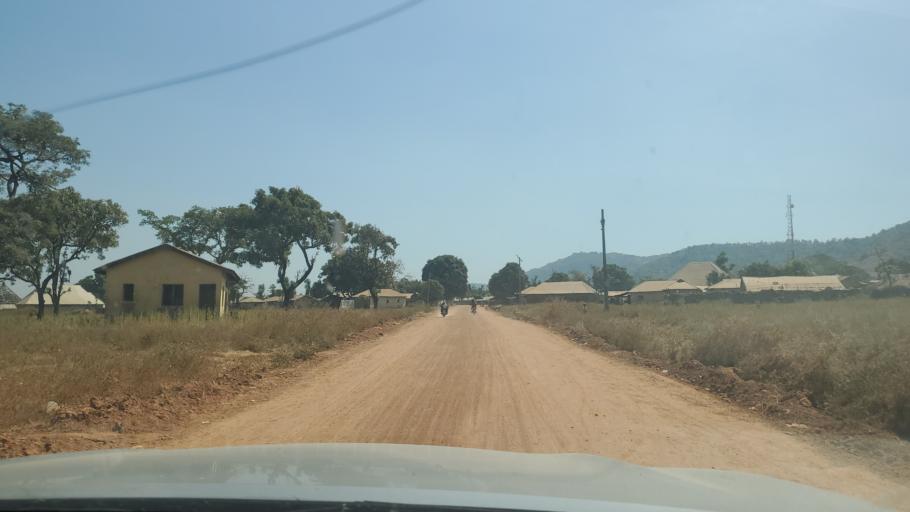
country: NG
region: Niger
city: Gawu Babangida
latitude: 9.2151
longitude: 6.8426
